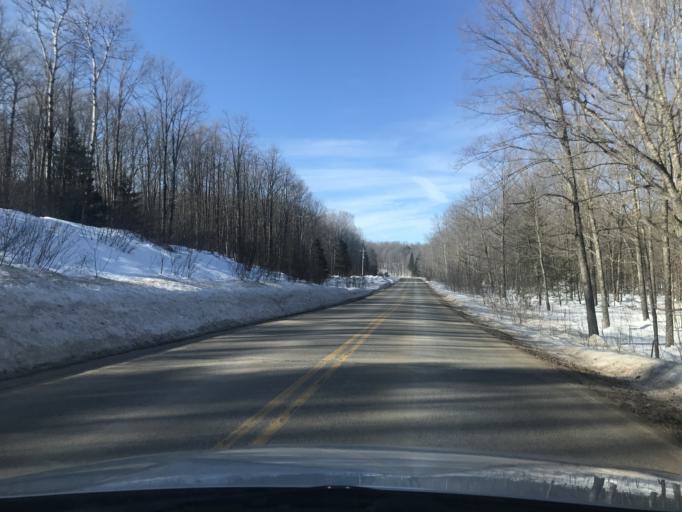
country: US
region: Michigan
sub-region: Dickinson County
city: Kingsford
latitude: 45.4193
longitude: -88.4107
